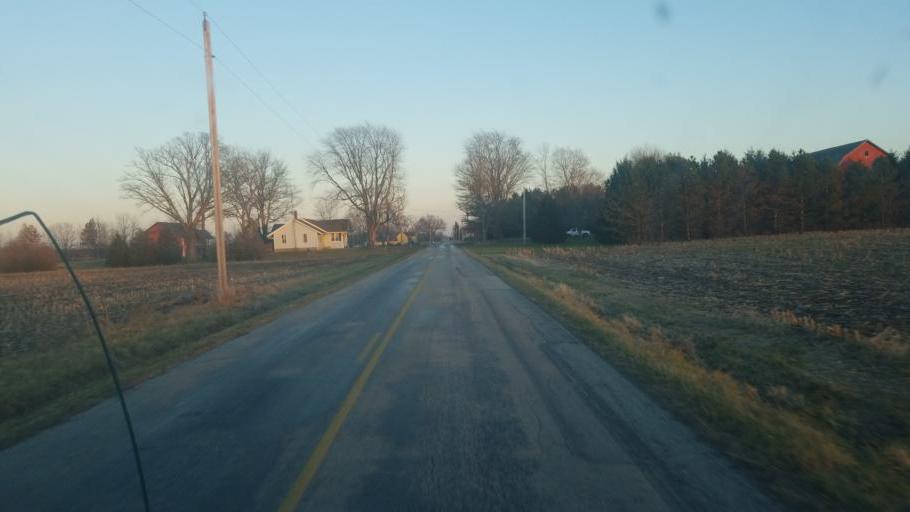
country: US
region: Ohio
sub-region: Marion County
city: Marion
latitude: 40.6222
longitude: -83.2925
